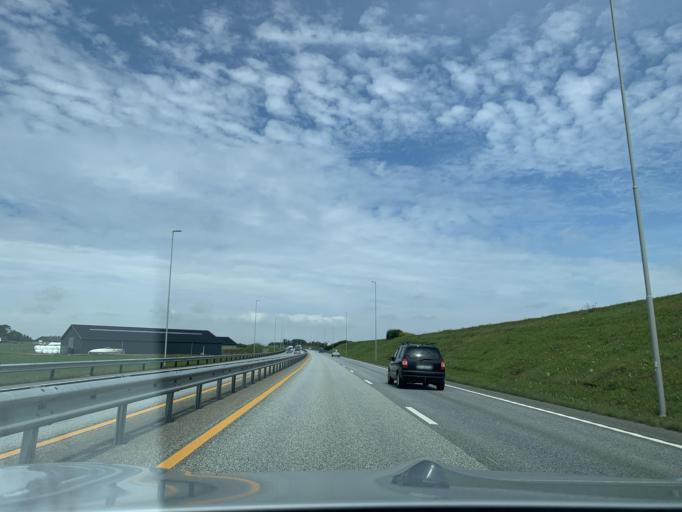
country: NO
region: Rogaland
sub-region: Sandnes
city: Sandnes
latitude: 58.8249
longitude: 5.7034
